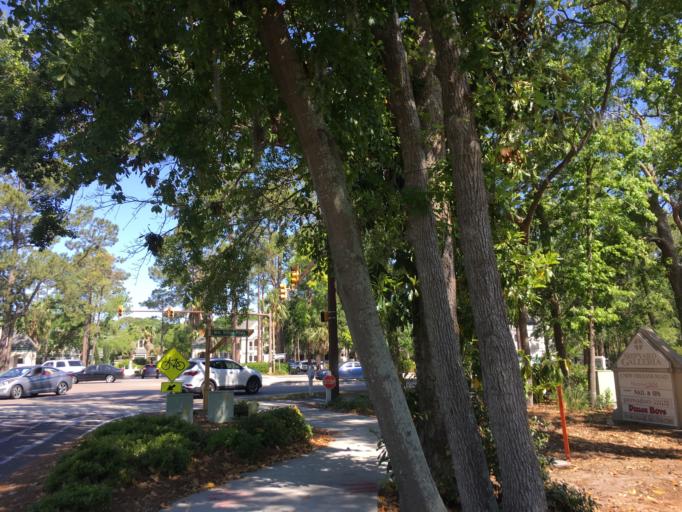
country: US
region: South Carolina
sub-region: Beaufort County
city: Hilton Head Island
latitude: 32.1590
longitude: -80.7531
